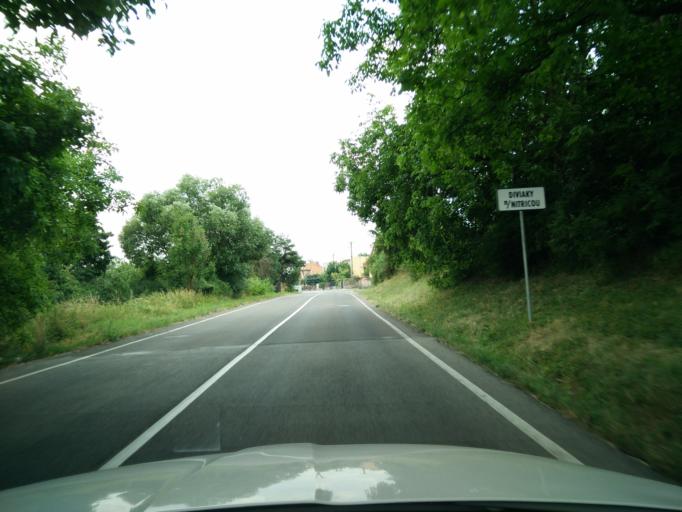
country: SK
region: Nitriansky
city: Novaky
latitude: 48.7692
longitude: 18.4913
